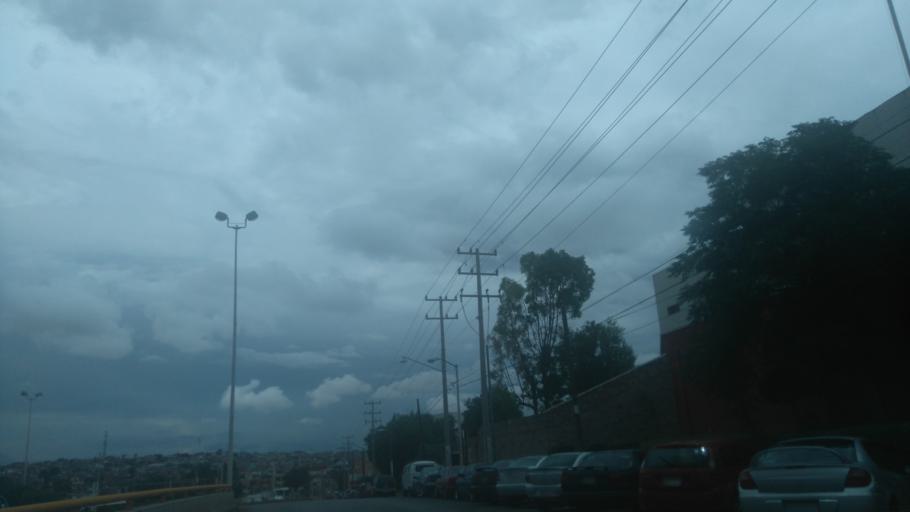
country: MX
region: Zacatecas
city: Zacatecas
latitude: 22.7621
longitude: -102.5782
